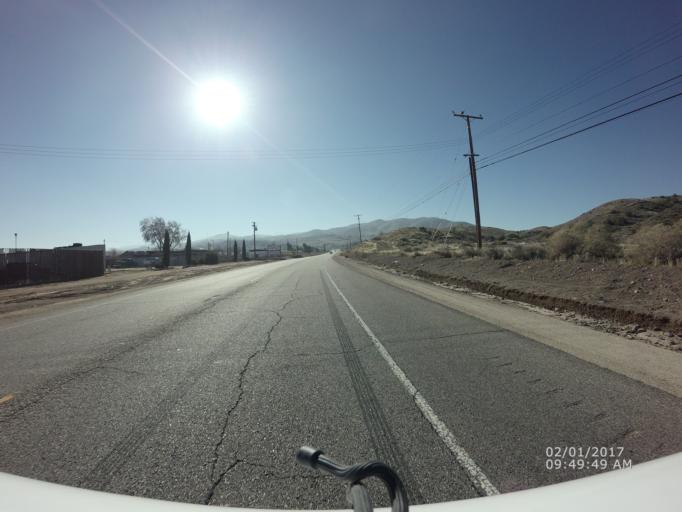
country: US
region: California
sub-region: Los Angeles County
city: Vincent
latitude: 34.5298
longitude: -118.0999
